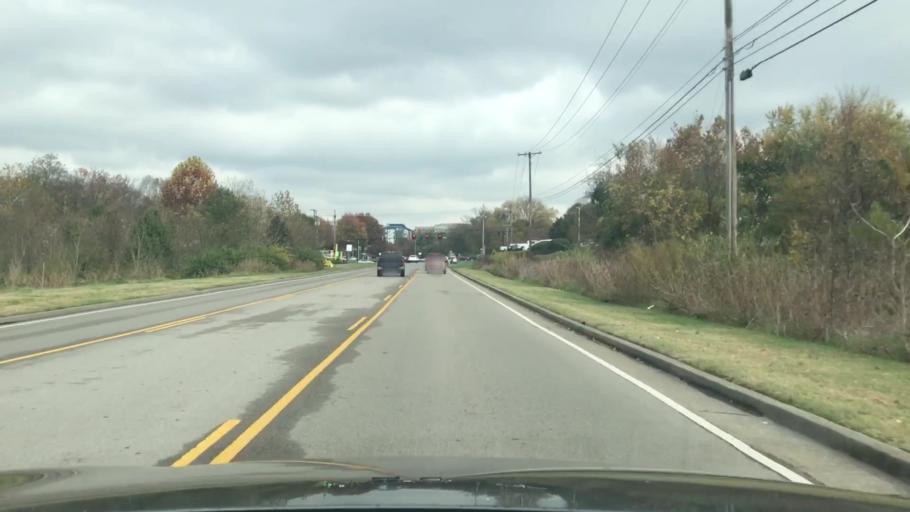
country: US
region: Tennessee
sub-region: Williamson County
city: Franklin
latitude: 35.9525
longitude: -86.8204
